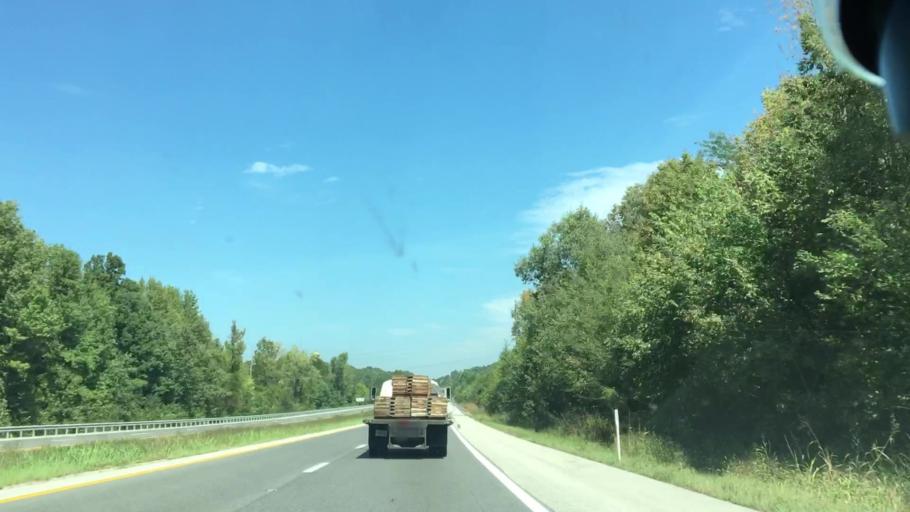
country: US
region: Kentucky
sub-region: Hopkins County
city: Madisonville
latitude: 37.3733
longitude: -87.4867
